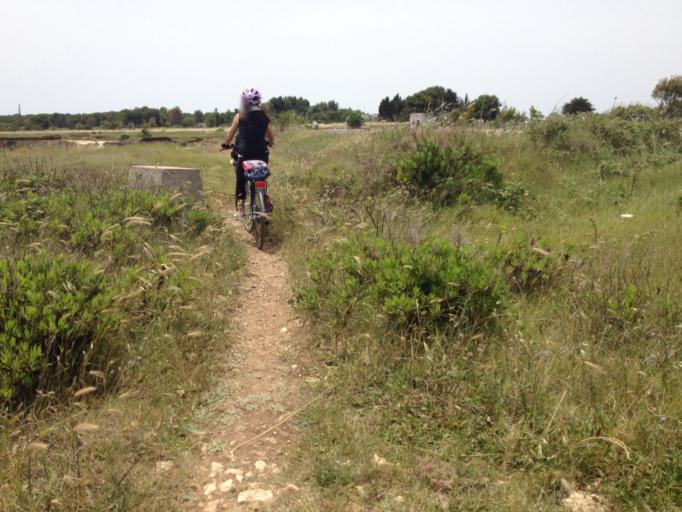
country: IT
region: Apulia
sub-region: Provincia di Lecce
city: Borgagne
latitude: 40.2594
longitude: 18.4419
